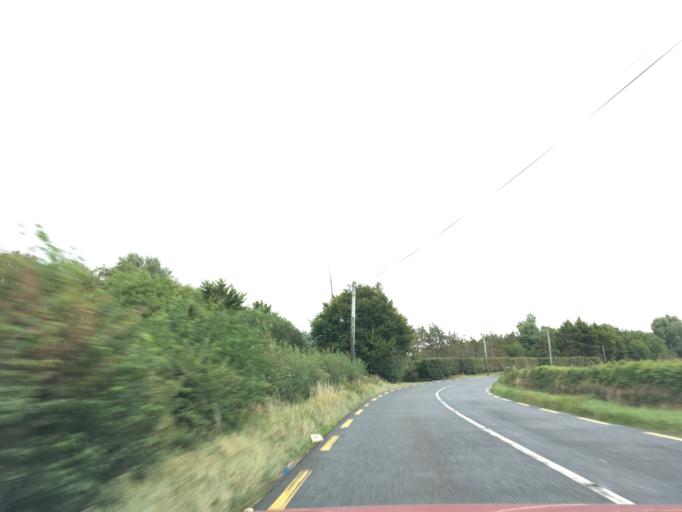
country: IE
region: Munster
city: Fethard
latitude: 52.4312
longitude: -7.7815
